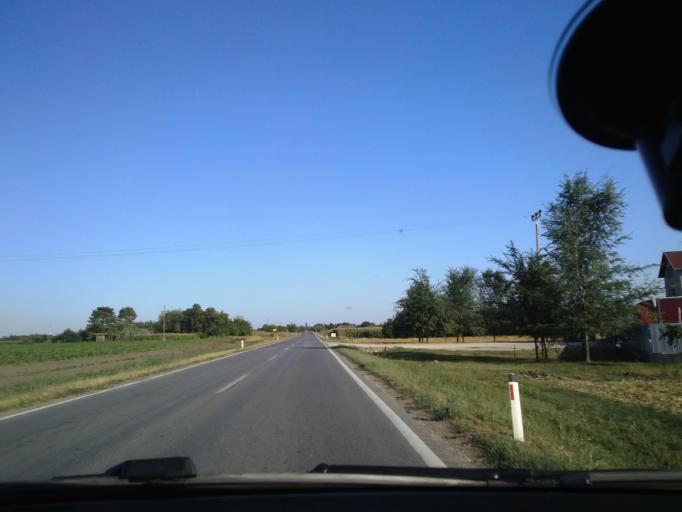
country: RS
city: Doroslovo
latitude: 45.6776
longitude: 19.1838
